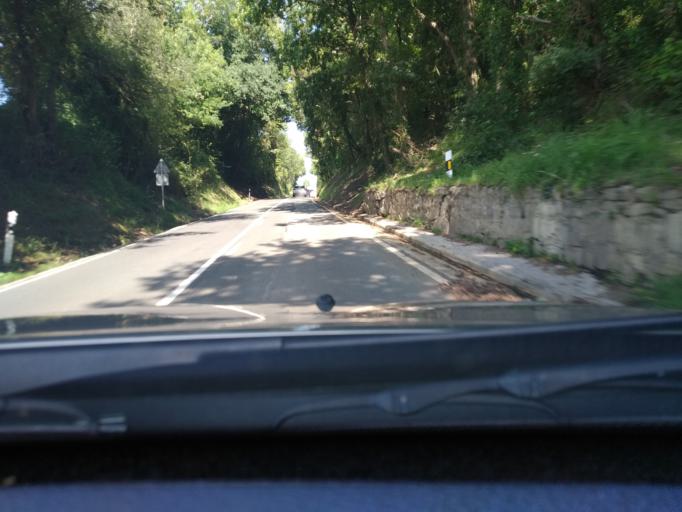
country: ES
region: Basque Country
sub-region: Bizkaia
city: Bakio
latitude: 43.4365
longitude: -2.7810
